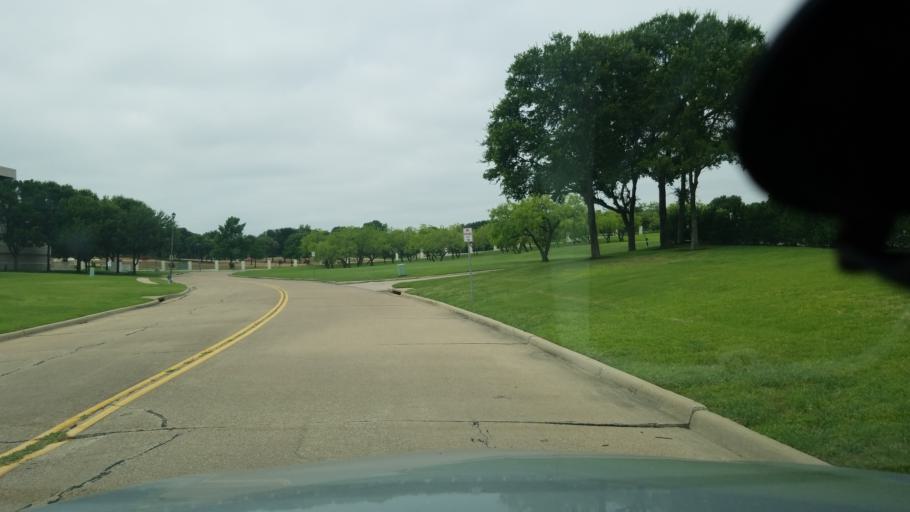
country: US
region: Texas
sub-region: Dallas County
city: Irving
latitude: 32.8590
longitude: -96.9356
